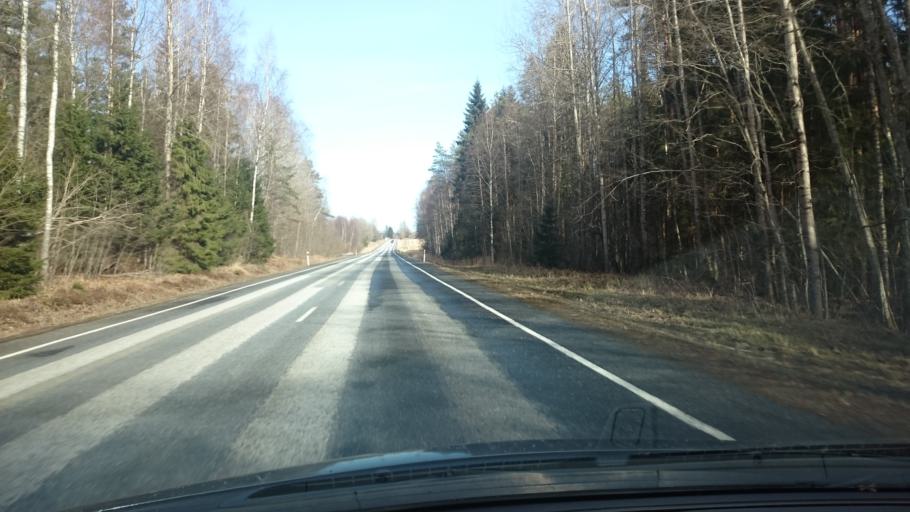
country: EE
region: Jaervamaa
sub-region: Tueri vald
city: Sarevere
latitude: 58.7451
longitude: 25.3099
